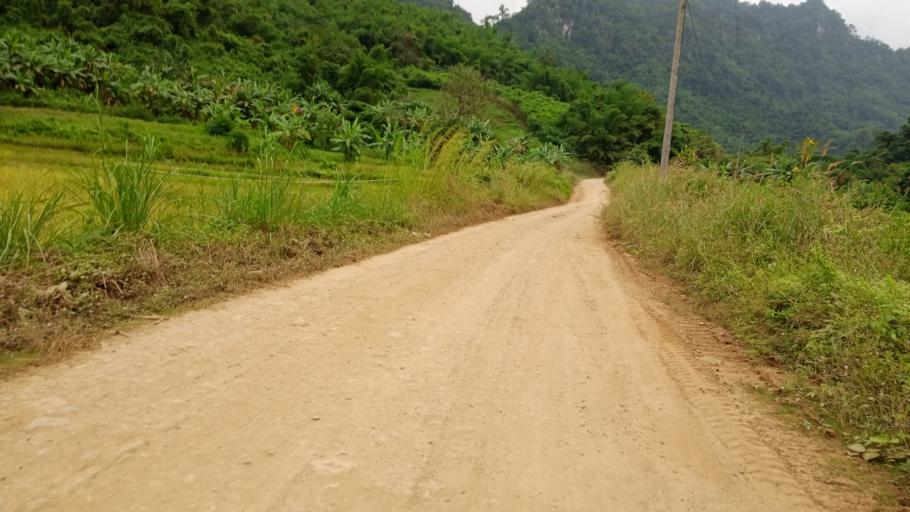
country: LA
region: Xiangkhoang
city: Phonsavan
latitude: 19.0931
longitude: 102.9956
